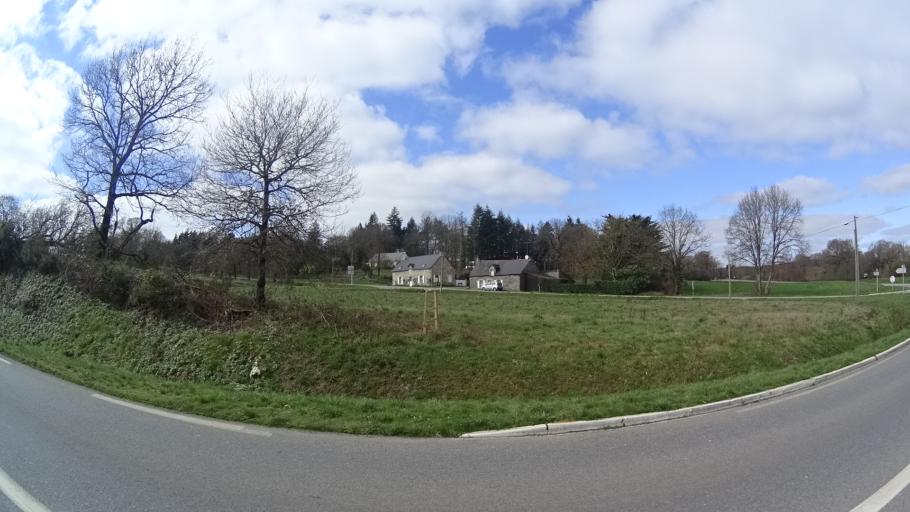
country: FR
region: Brittany
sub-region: Departement du Morbihan
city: Caro
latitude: 47.8374
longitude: -2.3106
